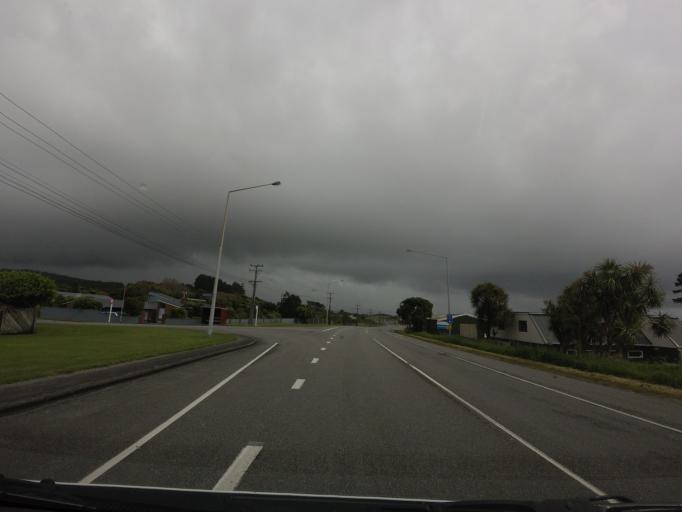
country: NZ
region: West Coast
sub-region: Grey District
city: Greymouth
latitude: -42.4865
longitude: 171.1816
